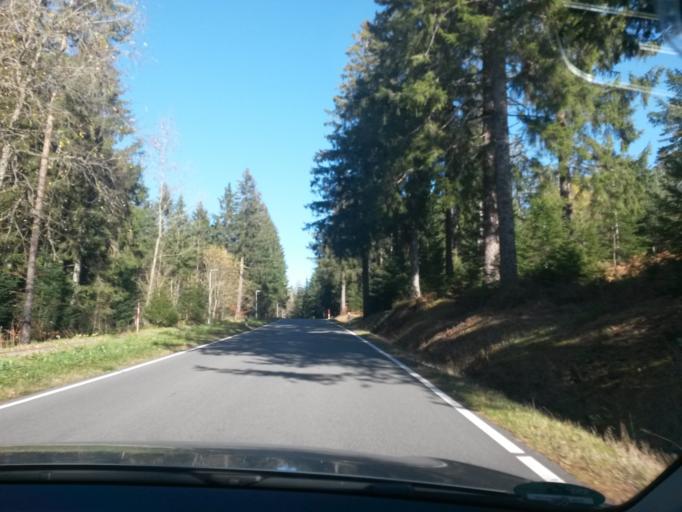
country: DE
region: Baden-Wuerttemberg
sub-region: Karlsruhe Region
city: Bad Rippoldsau-Schapbach
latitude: 48.4690
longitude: 8.2978
